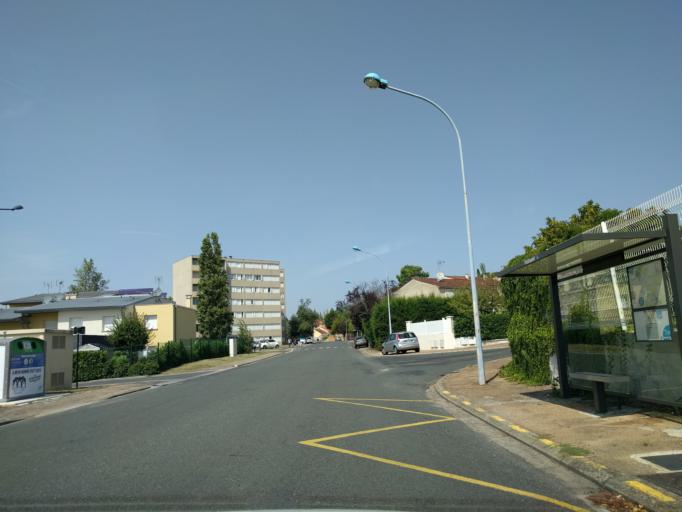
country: FR
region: Midi-Pyrenees
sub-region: Departement du Tarn
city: Castres
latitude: 43.5933
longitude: 2.2552
